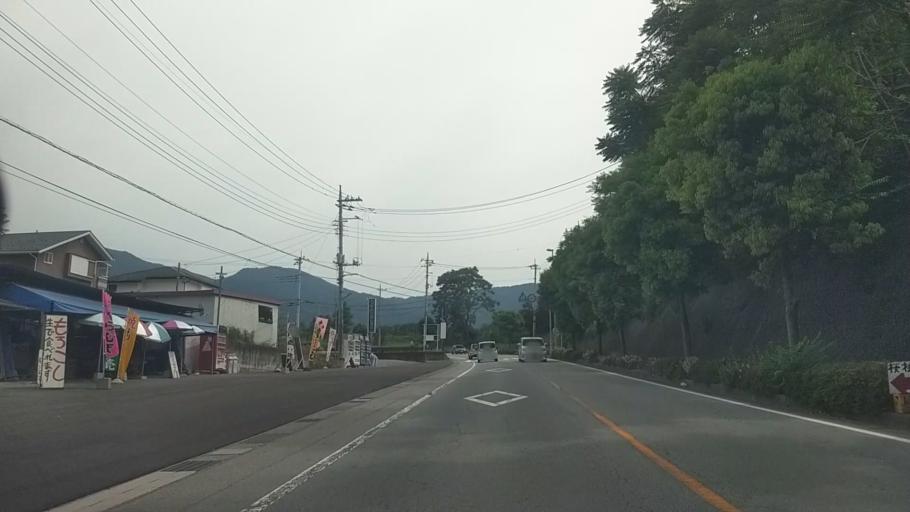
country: JP
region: Yamanashi
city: Isawa
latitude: 35.5870
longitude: 138.5901
